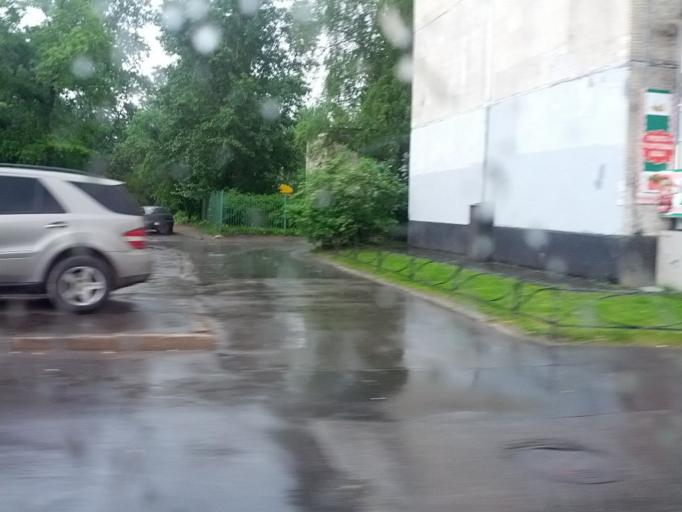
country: RU
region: St.-Petersburg
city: Obukhovo
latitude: 59.8831
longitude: 30.4693
